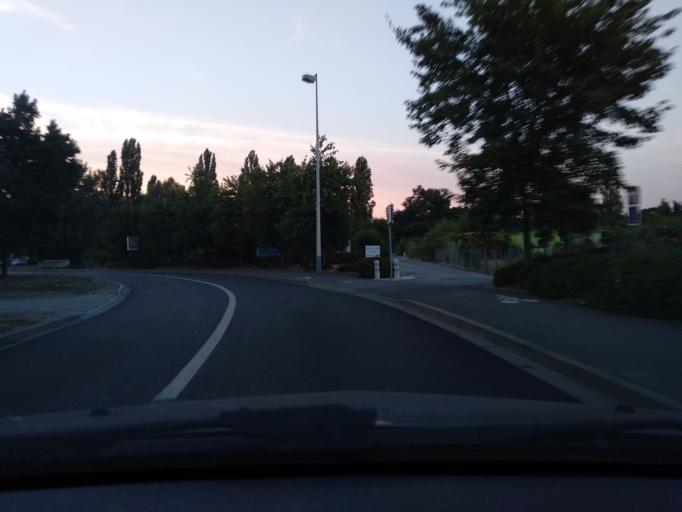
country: FR
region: Centre
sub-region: Departement d'Indre-et-Loire
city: Tours
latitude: 47.3632
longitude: 0.6896
